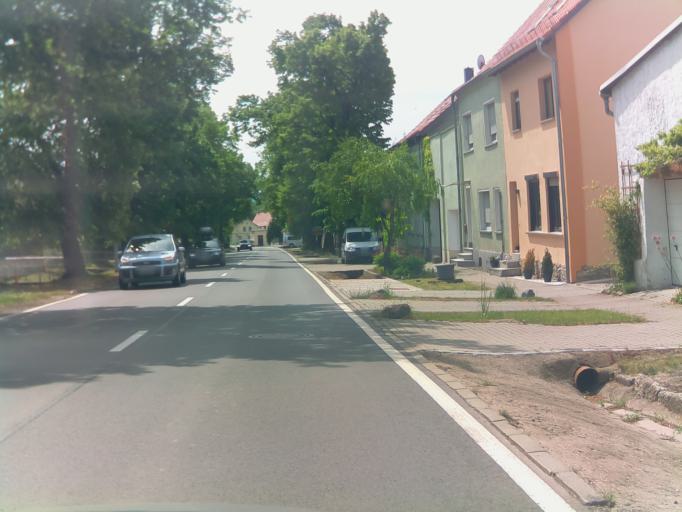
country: DE
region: Saxony-Anhalt
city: Hedersleben
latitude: 51.8596
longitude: 11.2562
